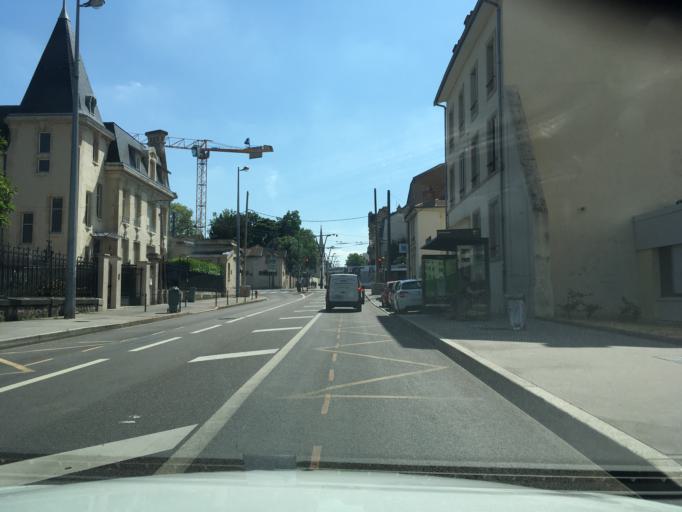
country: FR
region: Lorraine
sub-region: Departement de Meurthe-et-Moselle
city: Nancy
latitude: 48.6794
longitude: 6.1806
